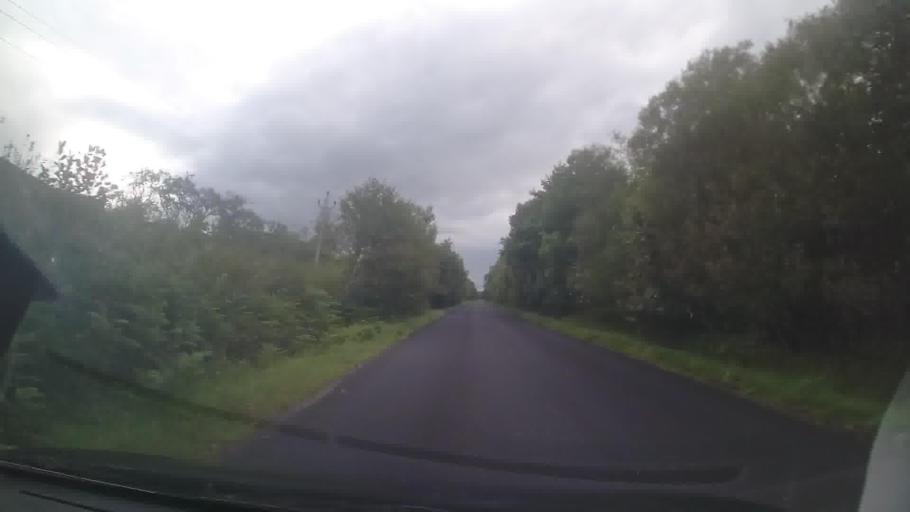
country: GB
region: Scotland
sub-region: Argyll and Bute
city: Garelochhead
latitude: 56.2396
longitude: -4.9576
